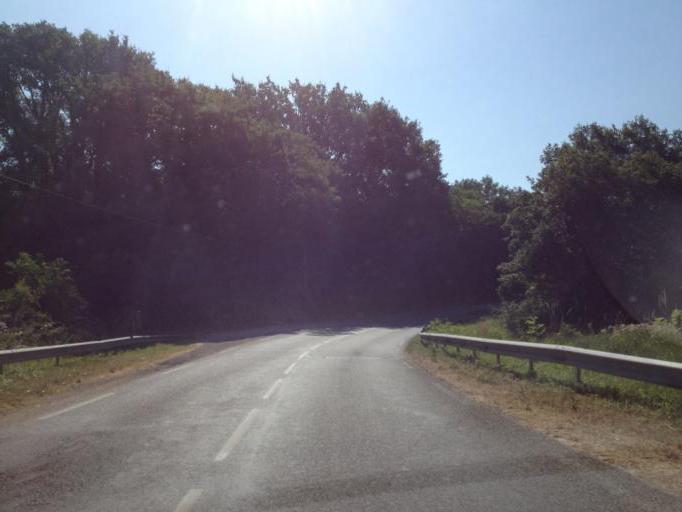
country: FR
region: Rhone-Alpes
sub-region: Departement de la Drome
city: Clerieux
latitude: 45.1314
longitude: 4.9531
